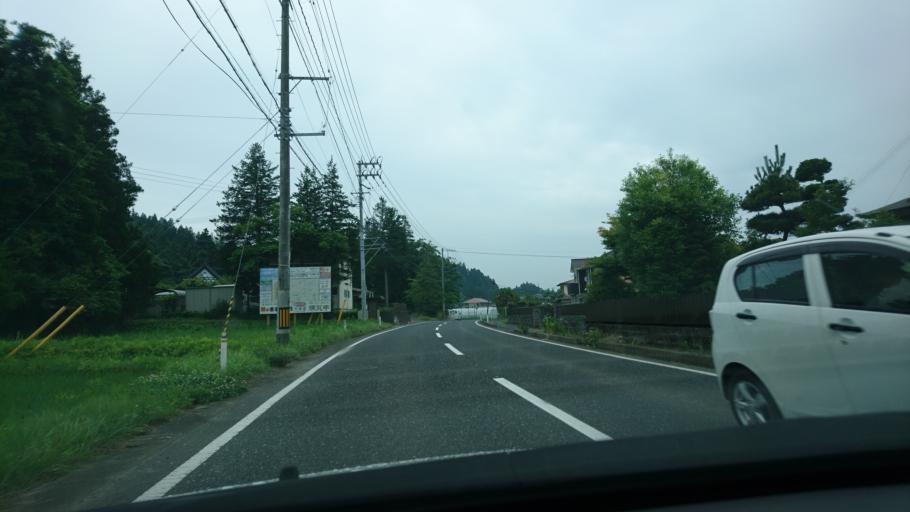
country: JP
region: Miyagi
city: Furukawa
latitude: 38.7301
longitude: 140.9873
